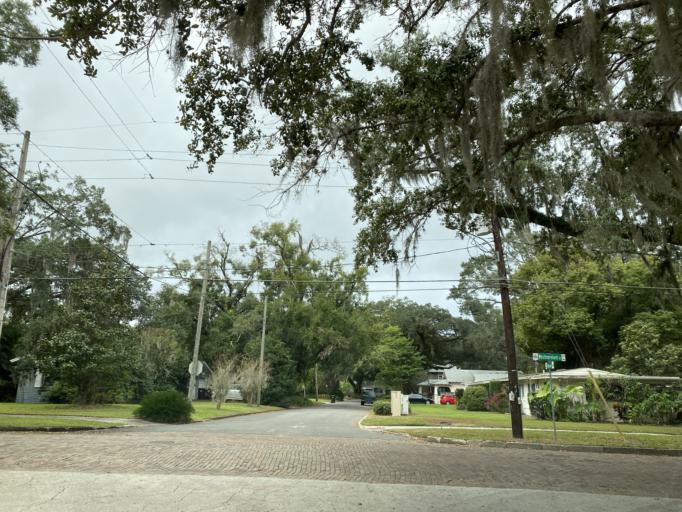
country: US
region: Florida
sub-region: Orange County
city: Orlando
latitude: 28.5559
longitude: -81.3932
